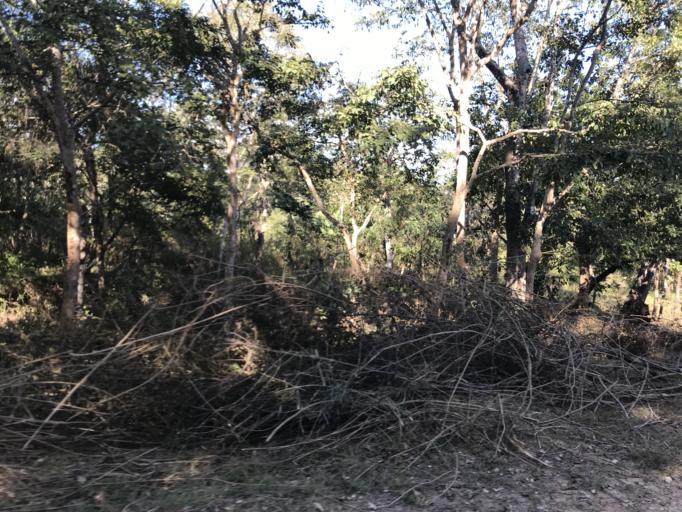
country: IN
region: Karnataka
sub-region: Mysore
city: Heggadadevankote
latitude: 11.9783
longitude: 76.2382
